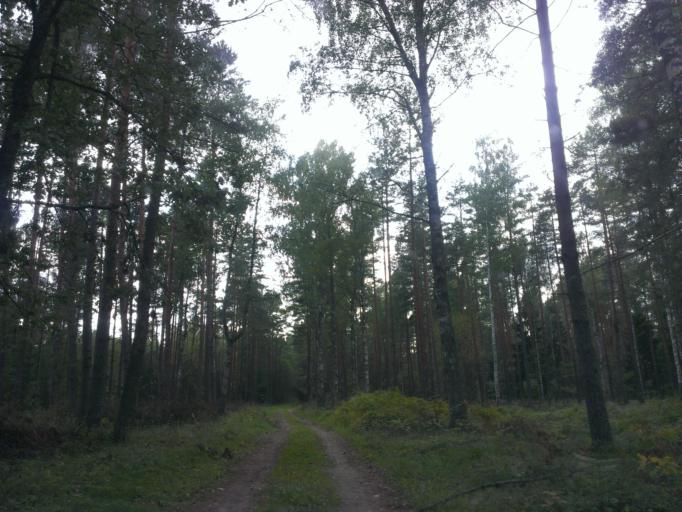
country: LV
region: Incukalns
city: Vangazi
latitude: 57.1070
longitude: 24.5330
